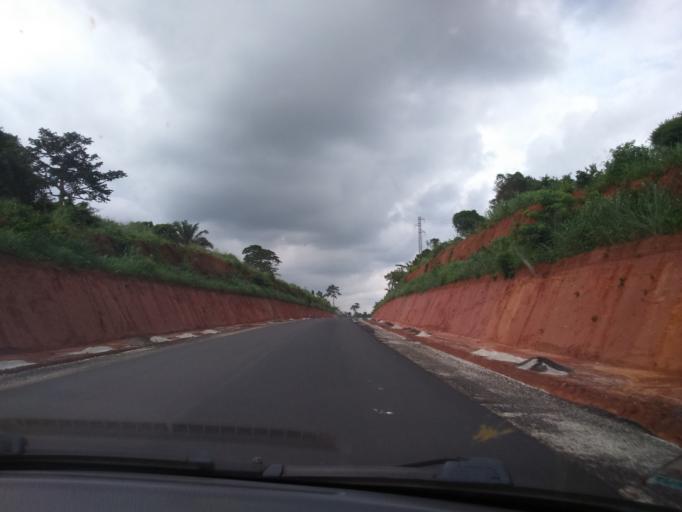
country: CI
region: Lagunes
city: Akoupe
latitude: 6.5025
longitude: -3.8242
